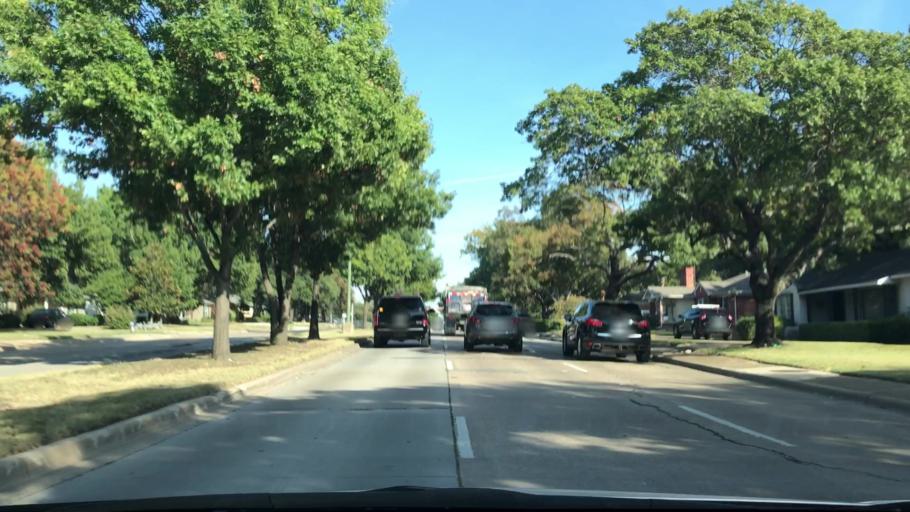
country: US
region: Texas
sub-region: Dallas County
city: University Park
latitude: 32.8798
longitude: -96.7891
